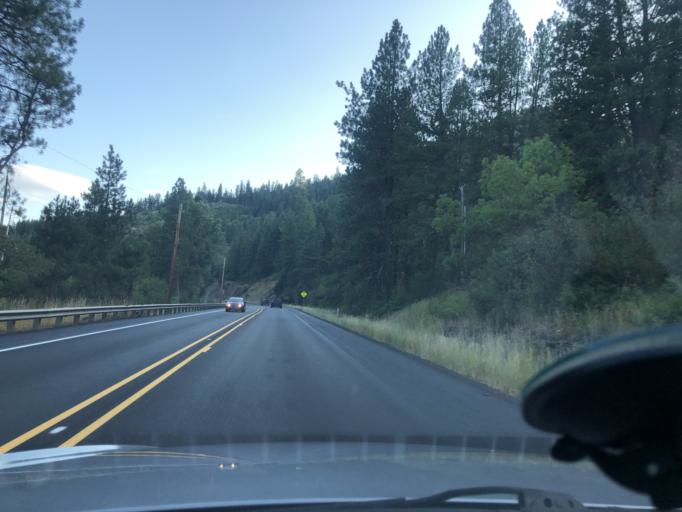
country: US
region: Washington
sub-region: Kittitas County
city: Cle Elum
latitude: 47.2457
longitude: -120.6962
